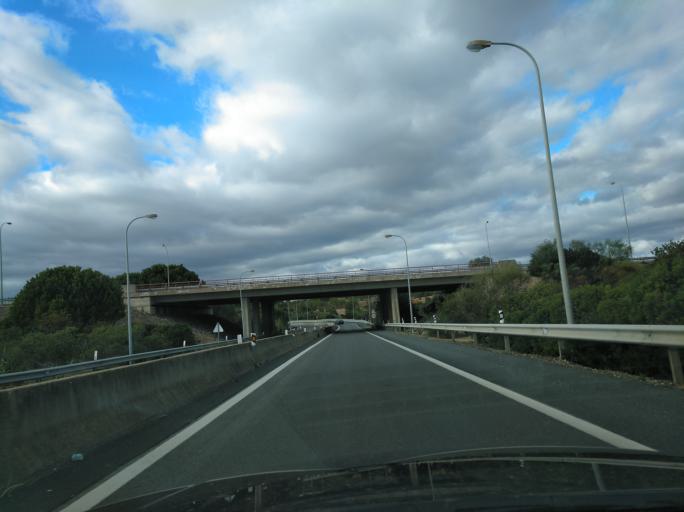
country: PT
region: Faro
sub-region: Tavira
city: Luz
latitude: 37.1367
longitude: -7.6944
